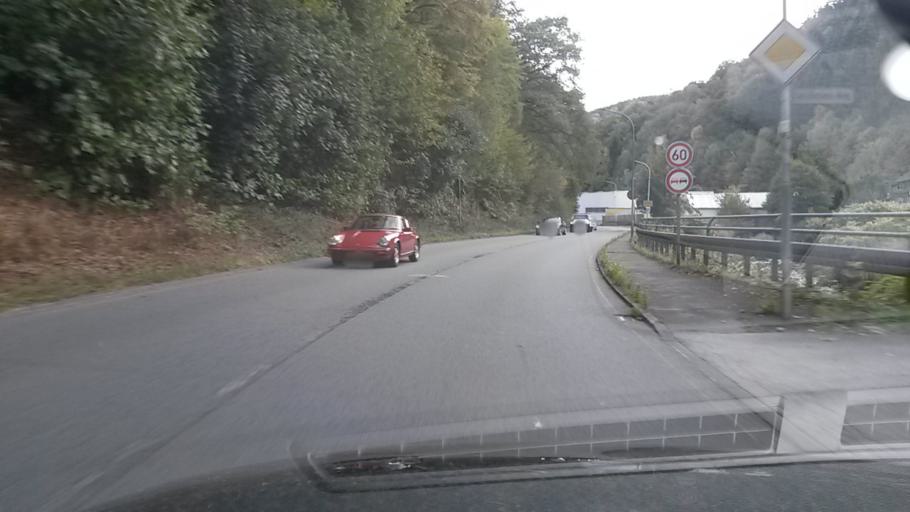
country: DE
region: North Rhine-Westphalia
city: Werdohl
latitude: 51.2353
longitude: 7.7242
